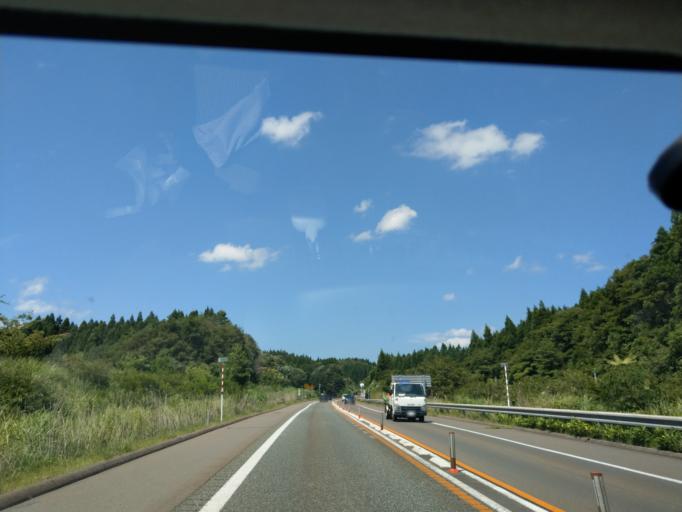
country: JP
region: Akita
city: Akita
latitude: 39.6746
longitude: 140.1867
